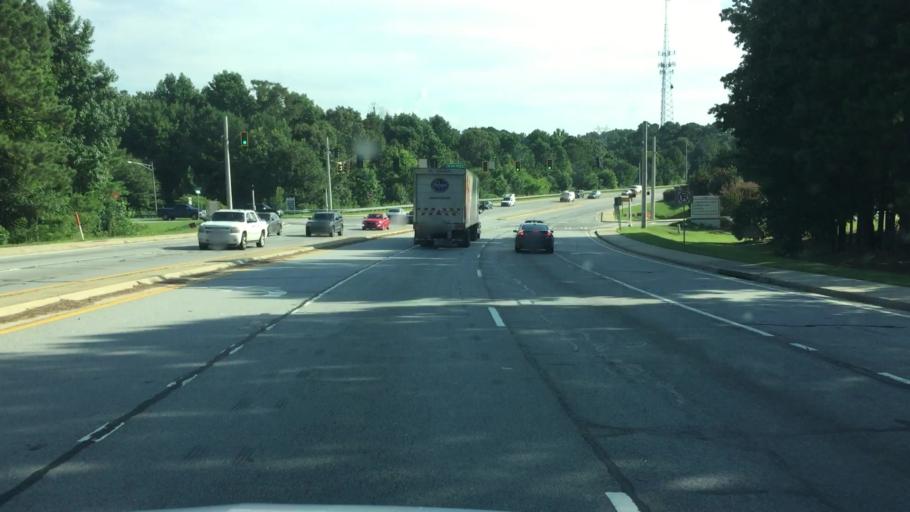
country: US
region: Georgia
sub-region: Rockdale County
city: Lakeview Estates
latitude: 33.7751
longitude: -84.0479
